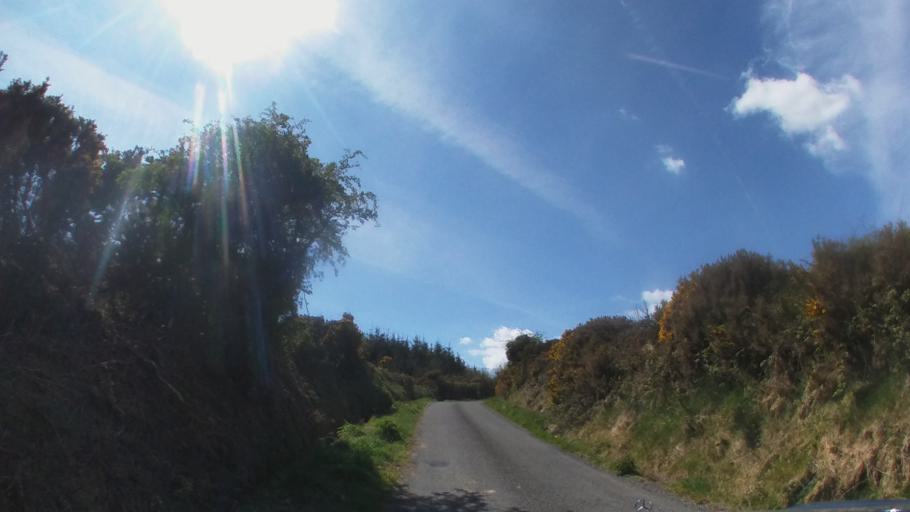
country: IE
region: Leinster
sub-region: Kilkenny
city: Callan
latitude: 52.6230
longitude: -7.5168
